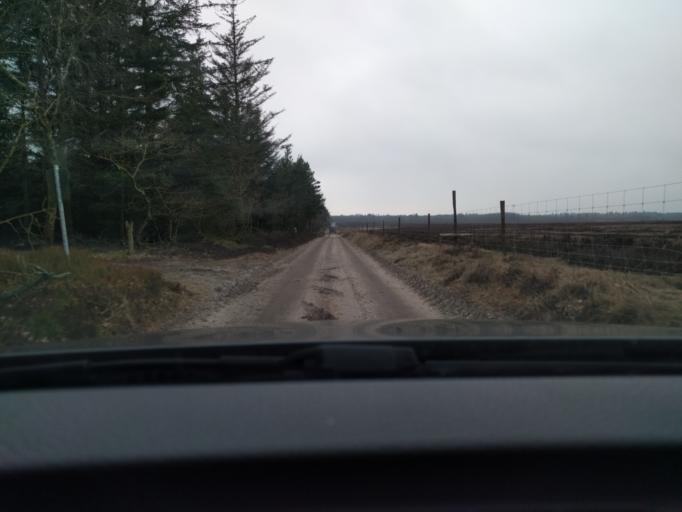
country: DK
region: Central Jutland
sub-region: Holstebro Kommune
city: Vinderup
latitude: 56.5002
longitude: 8.9220
